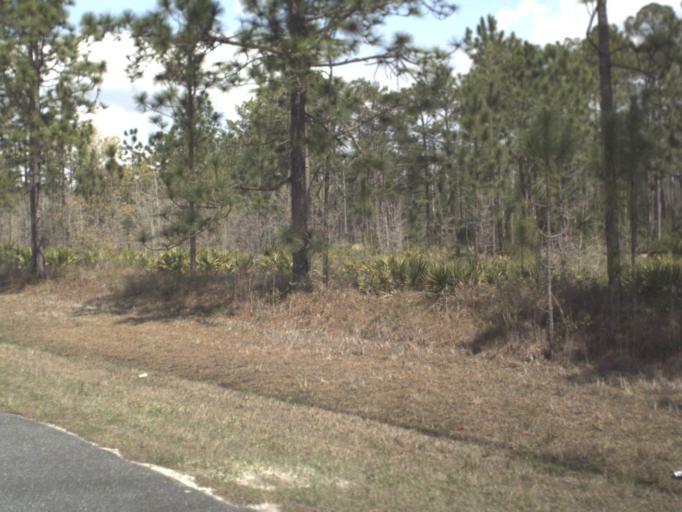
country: US
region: Florida
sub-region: Gulf County
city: Wewahitchka
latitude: 29.9961
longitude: -84.9771
